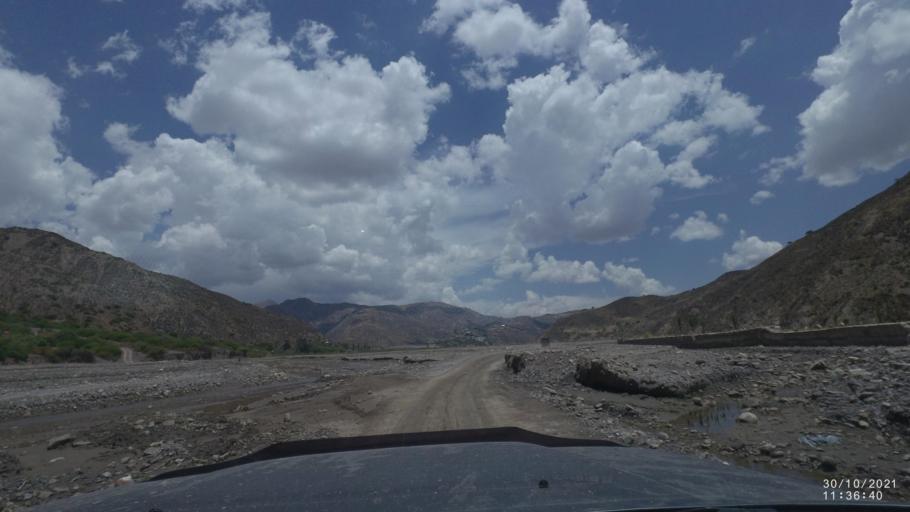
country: BO
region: Cochabamba
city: Sipe Sipe
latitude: -17.5230
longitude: -66.6039
